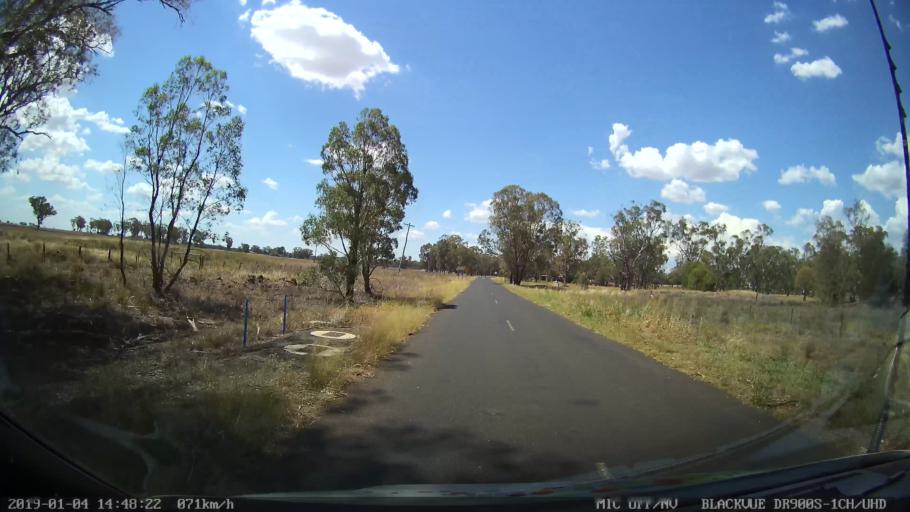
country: AU
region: New South Wales
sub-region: Dubbo Municipality
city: Dubbo
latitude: -32.0598
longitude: 148.6632
